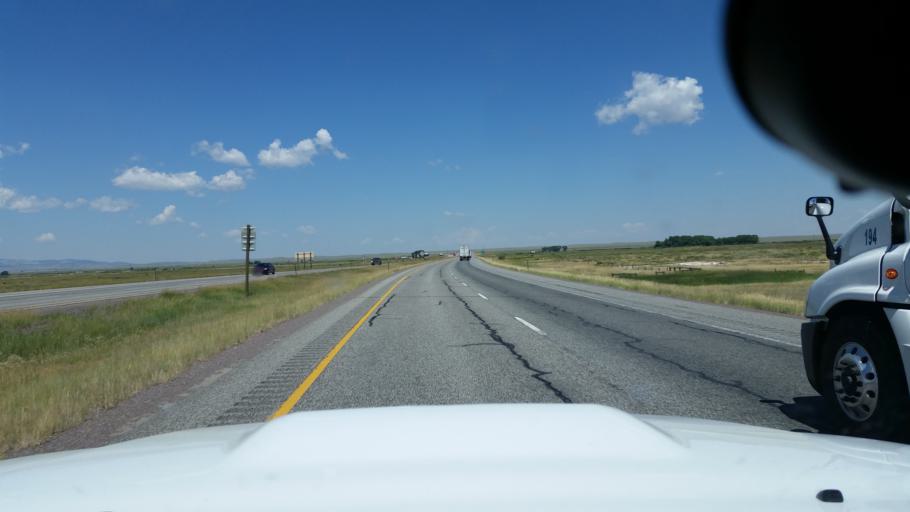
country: US
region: Wyoming
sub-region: Albany County
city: Laramie
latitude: 41.3837
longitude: -105.8145
